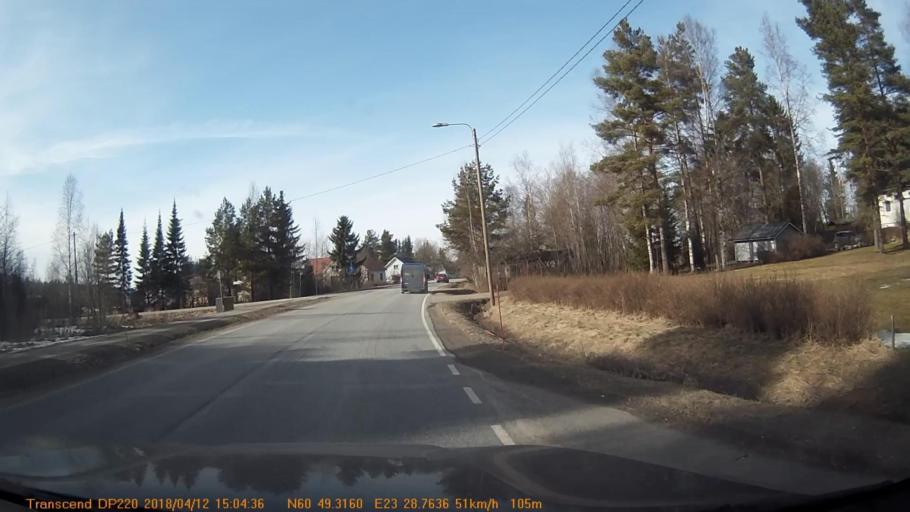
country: FI
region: Haeme
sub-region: Forssa
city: Jokioinen
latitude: 60.8221
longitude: 23.4792
